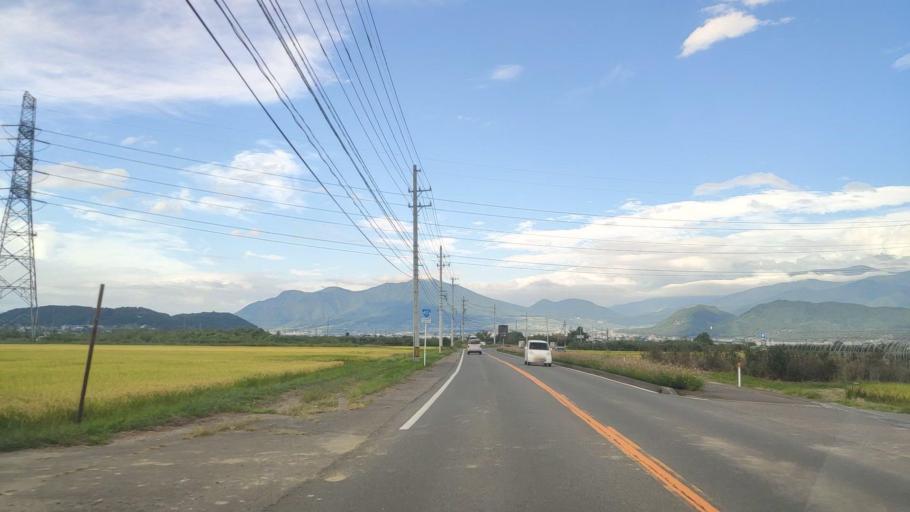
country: JP
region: Nagano
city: Nakano
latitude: 36.7207
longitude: 138.3291
